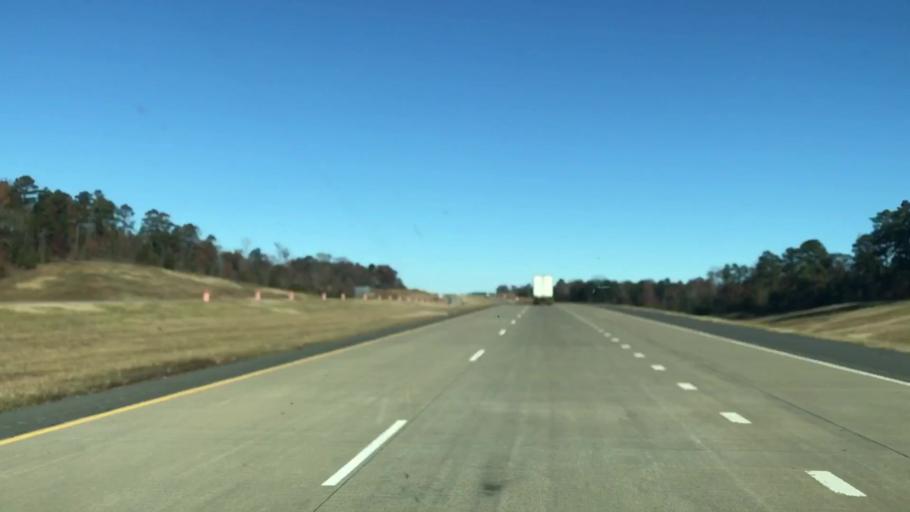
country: US
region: Louisiana
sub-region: Caddo Parish
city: Vivian
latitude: 32.9478
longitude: -93.8985
